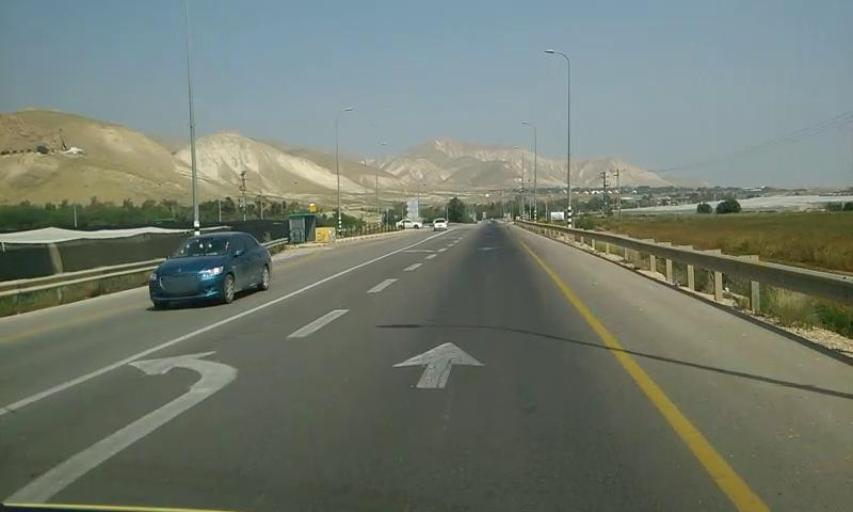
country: PS
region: West Bank
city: Al Fasayil
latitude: 32.0479
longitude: 35.4636
